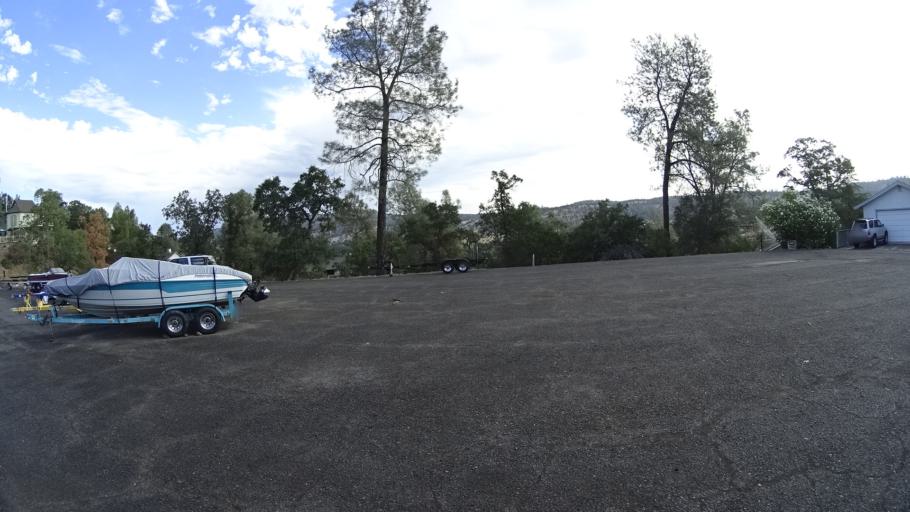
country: US
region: California
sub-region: Calaveras County
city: Copperopolis
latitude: 37.9134
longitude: -120.6028
